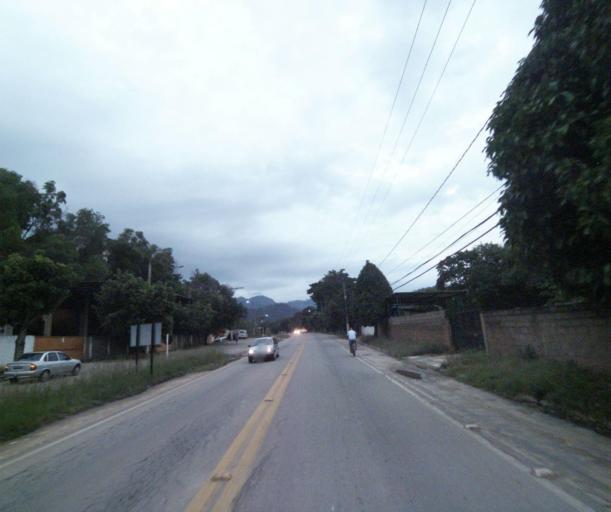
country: BR
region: Espirito Santo
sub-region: Castelo
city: Castelo
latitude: -20.6346
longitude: -41.2069
